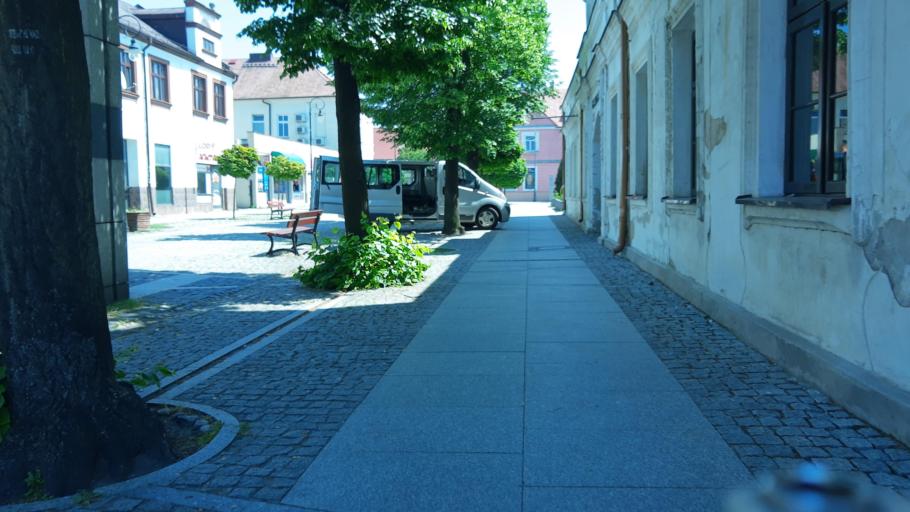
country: PL
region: Lodz Voivodeship
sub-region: Powiat sieradzki
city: Sieradz
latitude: 51.5941
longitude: 18.7362
